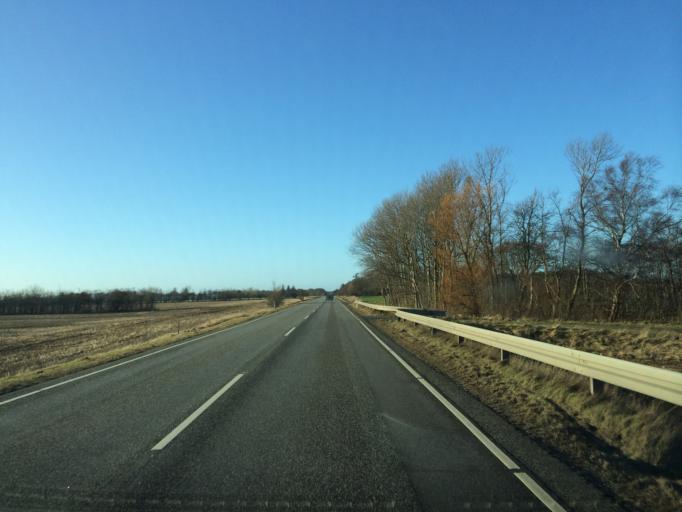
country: DK
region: Central Jutland
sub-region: Ringkobing-Skjern Kommune
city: Ringkobing
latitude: 56.1140
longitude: 8.3084
